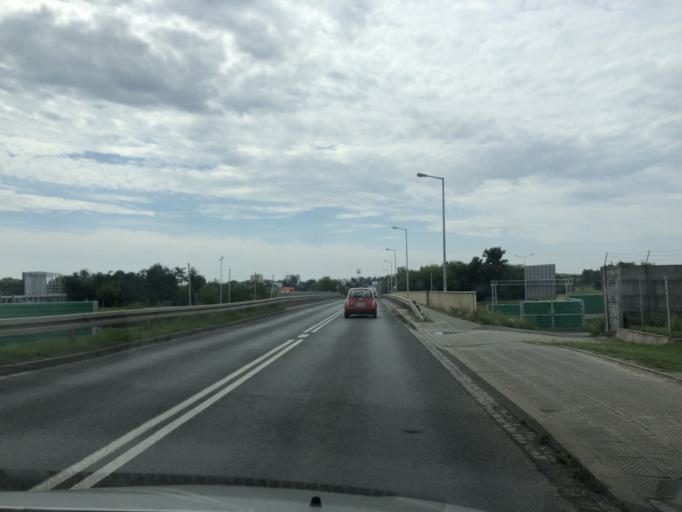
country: PL
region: Greater Poland Voivodeship
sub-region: Powiat poznanski
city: Lubon
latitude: 52.3554
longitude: 16.8840
